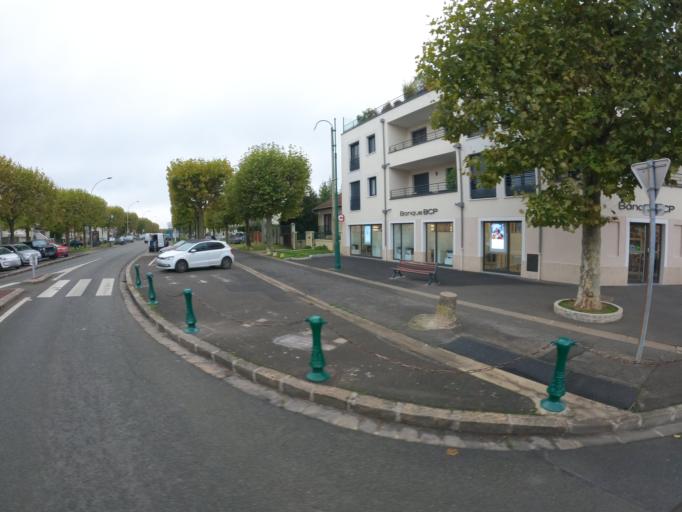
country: FR
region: Ile-de-France
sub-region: Departement du Val-de-Marne
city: Ormesson-sur-Marne
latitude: 48.7887
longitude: 2.5360
